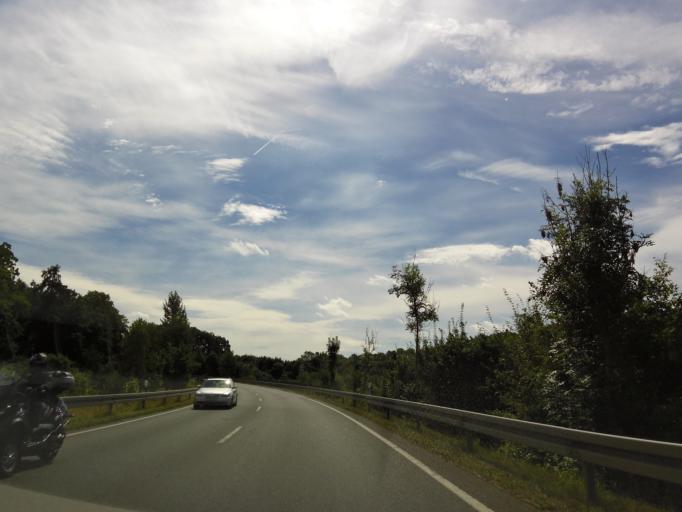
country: DE
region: Lower Saxony
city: Furstenberg
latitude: 51.7072
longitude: 9.3773
